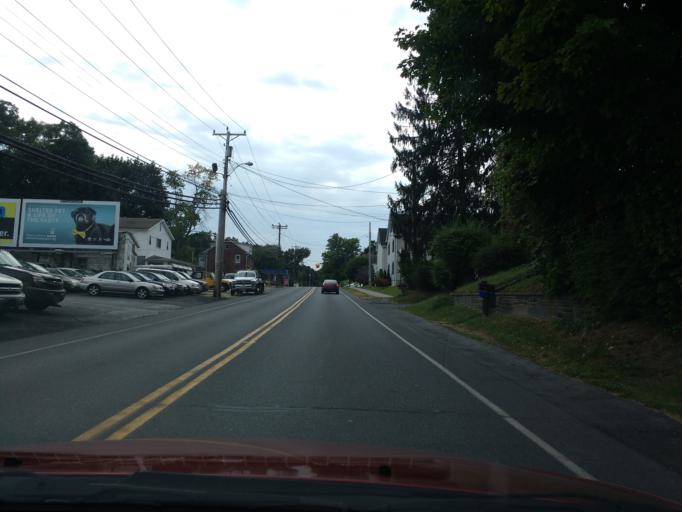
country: US
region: New York
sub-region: Ulster County
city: Lincoln Park
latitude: 41.9382
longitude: -73.9855
